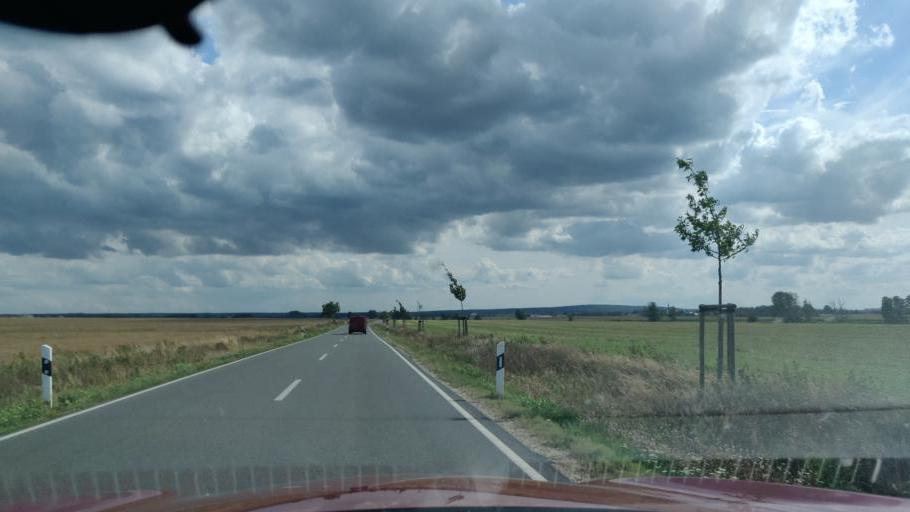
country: DE
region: Saxony
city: Schildau
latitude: 51.5067
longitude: 12.9106
